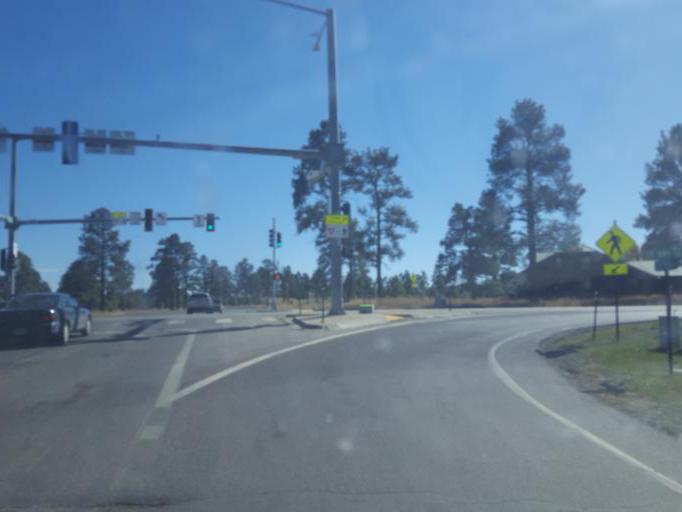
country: US
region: Colorado
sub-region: Archuleta County
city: Pagosa Springs
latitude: 37.2545
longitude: -107.0783
